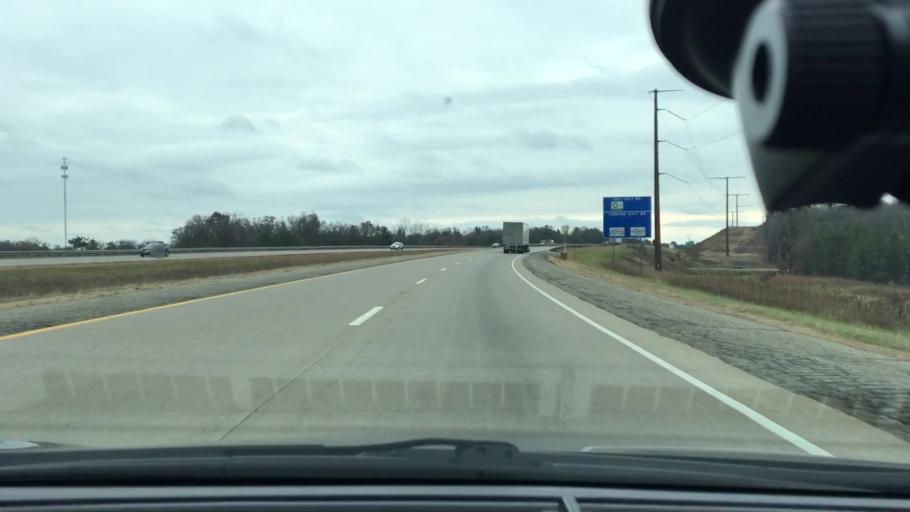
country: US
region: Wisconsin
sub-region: Columbia County
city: Wisconsin Dells
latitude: 43.6599
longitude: -89.8123
